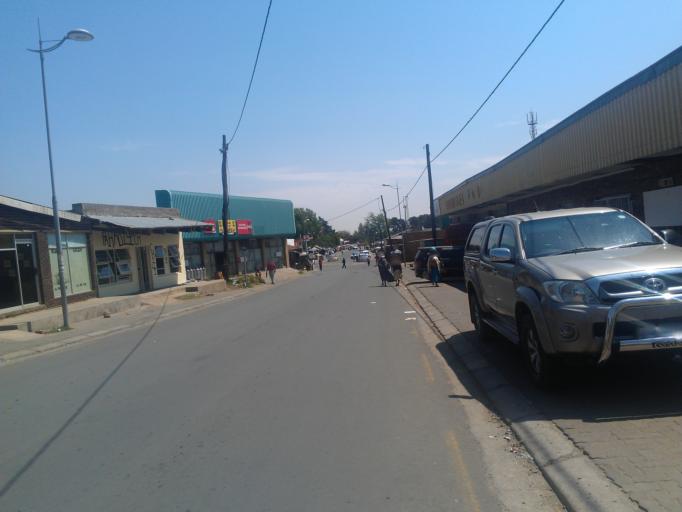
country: LS
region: Berea
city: Teyateyaneng
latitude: -29.1520
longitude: 27.7429
